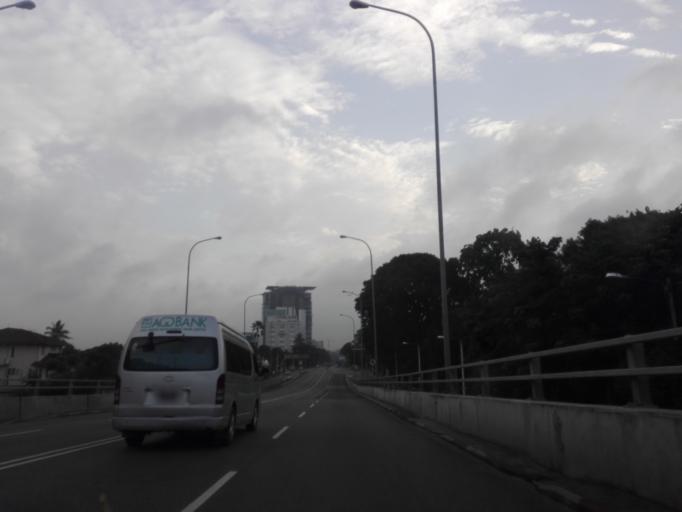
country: MM
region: Yangon
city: Yangon
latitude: 16.8286
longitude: 96.1315
